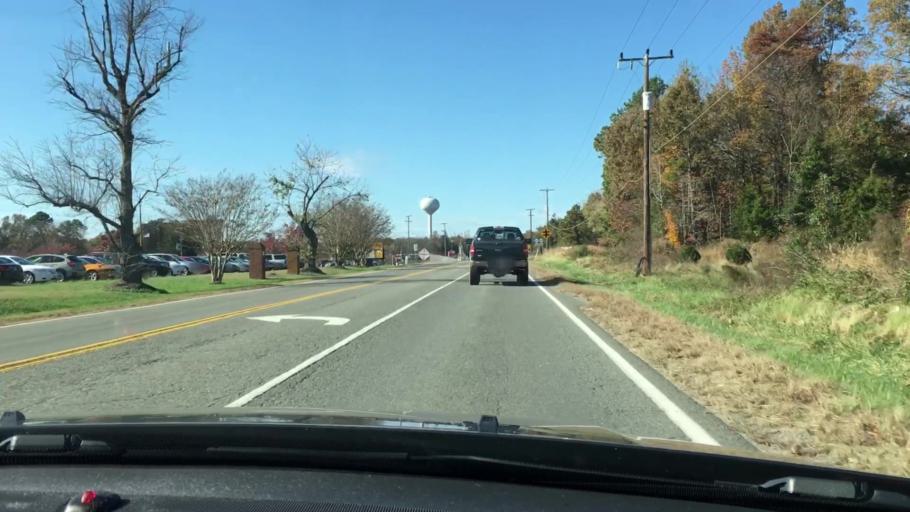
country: US
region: Virginia
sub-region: King William County
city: Central Garage
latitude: 37.7426
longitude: -77.1288
